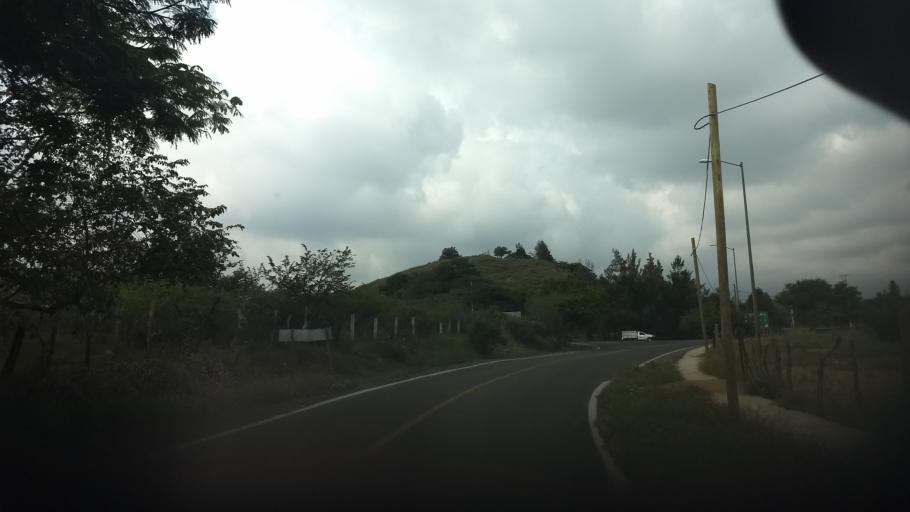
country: MX
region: Colima
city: Cofradia
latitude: 19.3972
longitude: -103.5344
